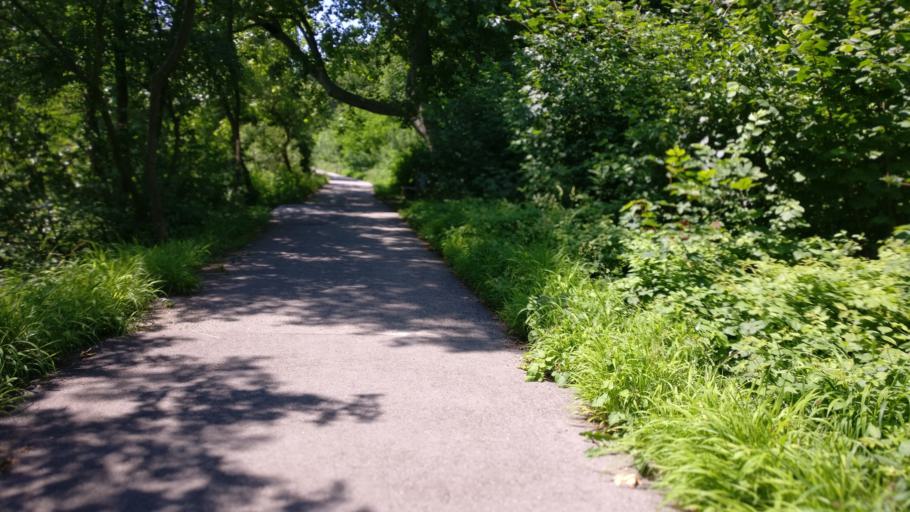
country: AT
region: Lower Austria
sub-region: Politischer Bezirk Baden
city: Oberwaltersdorf
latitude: 47.9703
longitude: 16.3152
